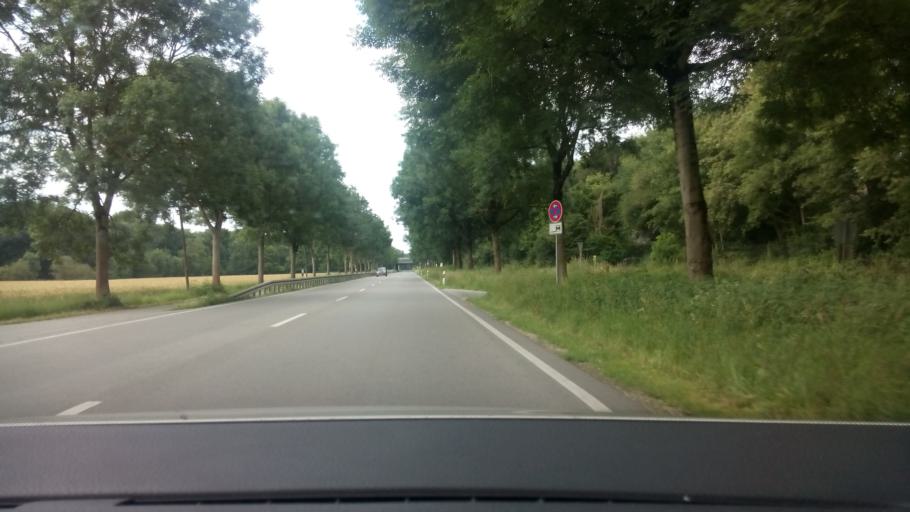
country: DE
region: Bavaria
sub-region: Upper Bavaria
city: Garching bei Munchen
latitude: 48.2220
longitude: 11.6383
